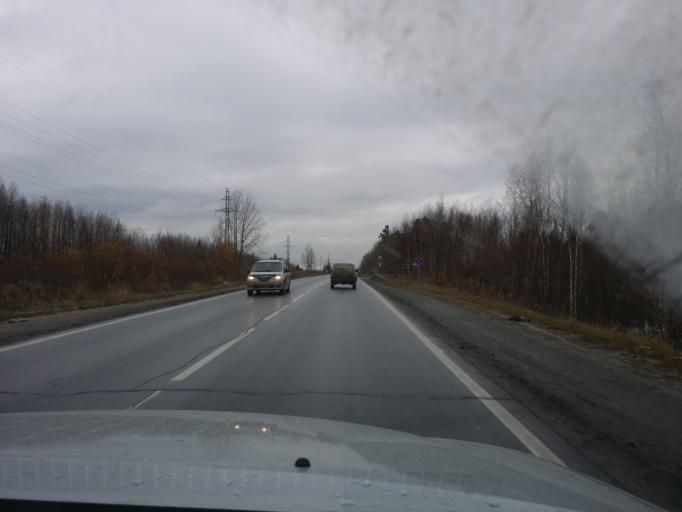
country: RU
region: Khanty-Mansiyskiy Avtonomnyy Okrug
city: Megion
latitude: 61.1059
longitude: 75.9225
